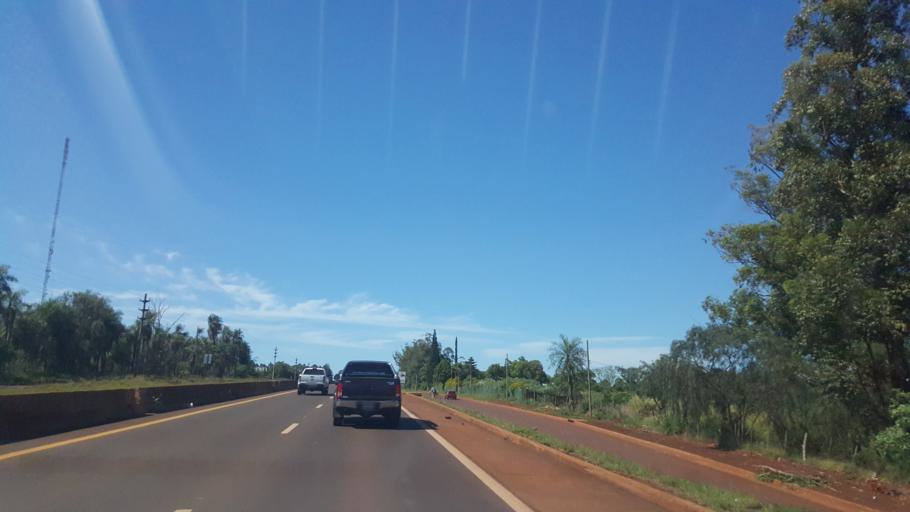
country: AR
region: Misiones
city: Garupa
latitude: -27.4744
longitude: -55.8634
